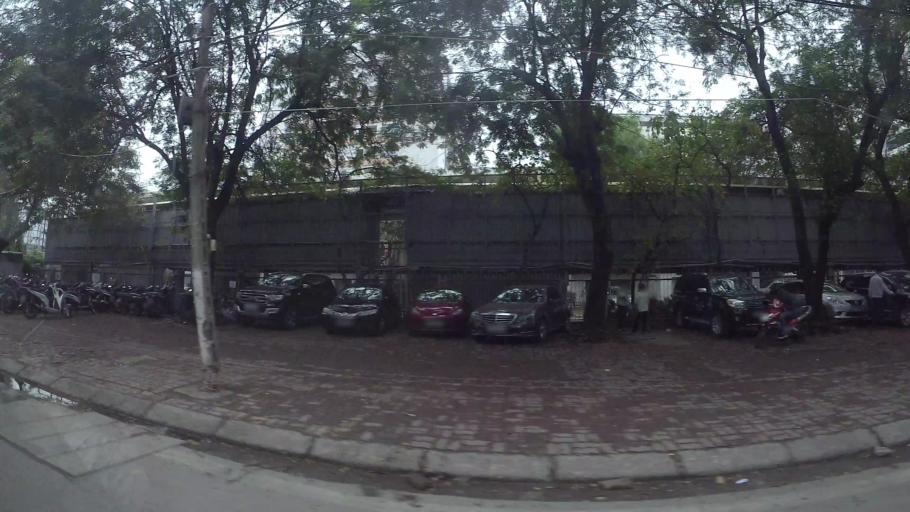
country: VN
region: Ha Noi
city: Hai BaTrung
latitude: 21.0042
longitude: 105.8405
